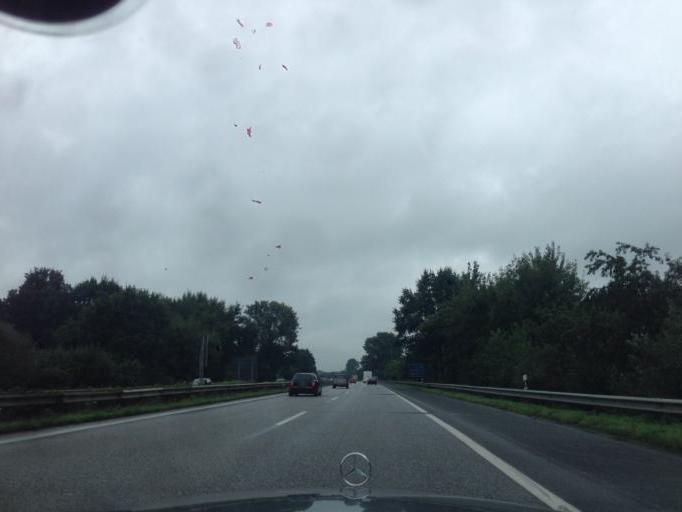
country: DE
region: Schleswig-Holstein
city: Nutzen
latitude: 53.8556
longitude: 9.9416
